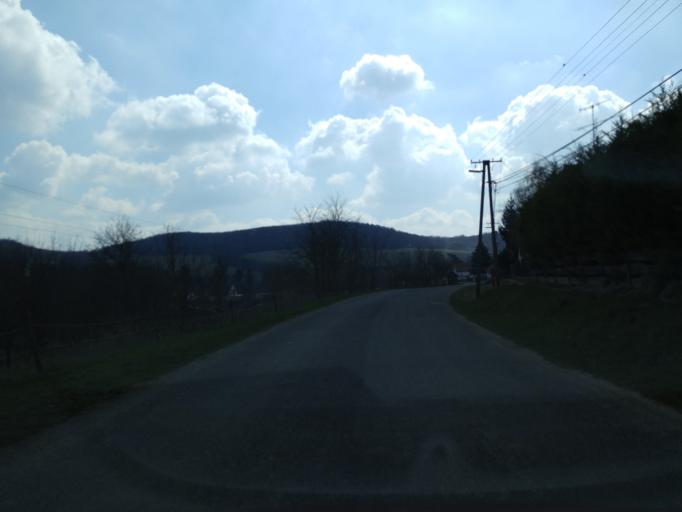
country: HU
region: Somogy
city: Adand
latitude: 46.8069
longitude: 18.1090
